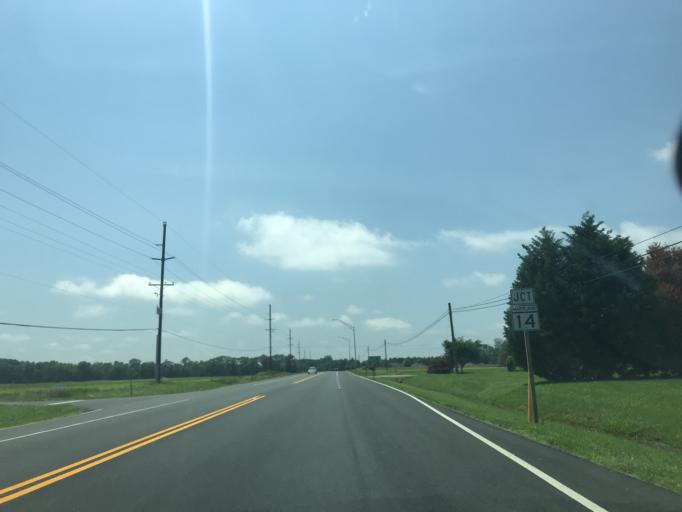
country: US
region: Maryland
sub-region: Dorchester County
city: Hurlock
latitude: 38.5914
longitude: -75.9482
